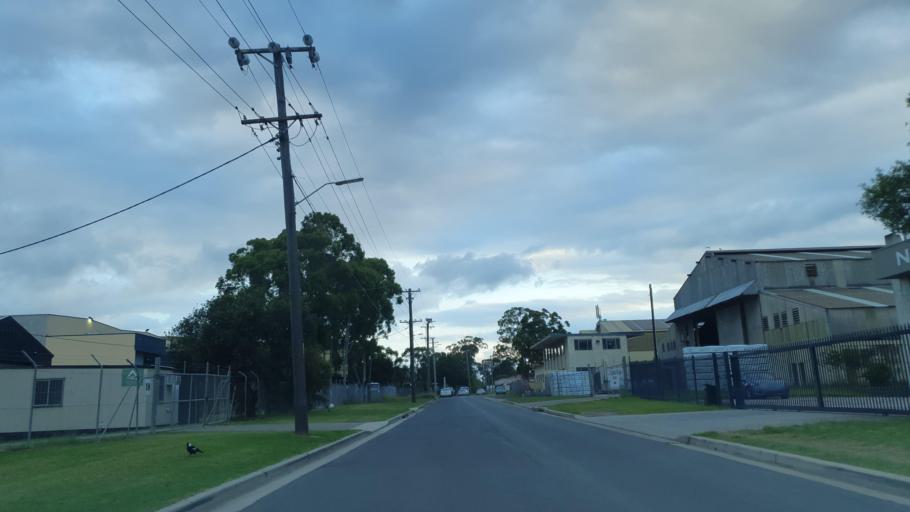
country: AU
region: New South Wales
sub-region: Penrith Municipality
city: Werrington County
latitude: -33.7400
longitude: 150.7726
